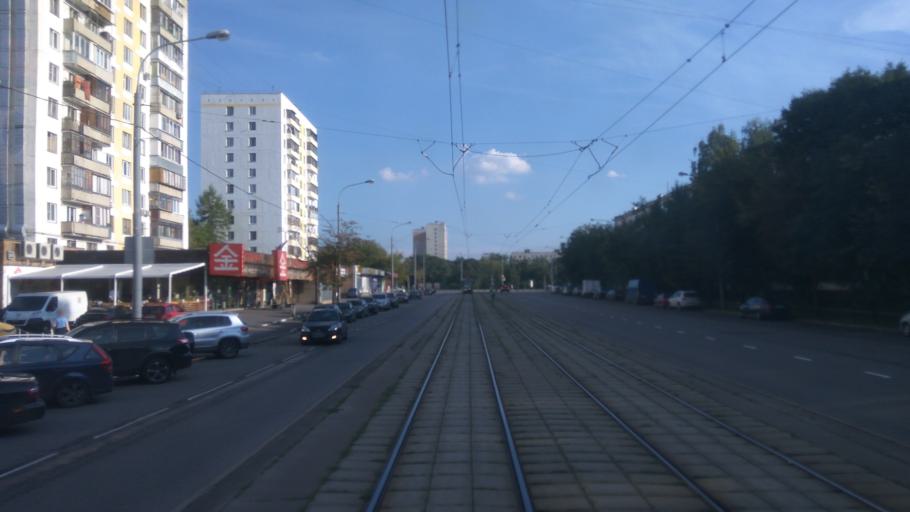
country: RU
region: Moscow
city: Perovo
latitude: 55.7538
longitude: 37.7907
